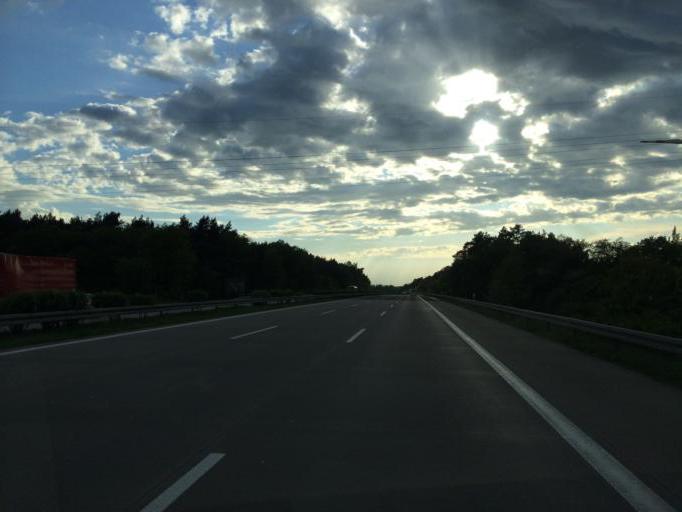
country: DE
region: Brandenburg
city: Brandenburg an der Havel
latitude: 52.3513
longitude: 12.5615
